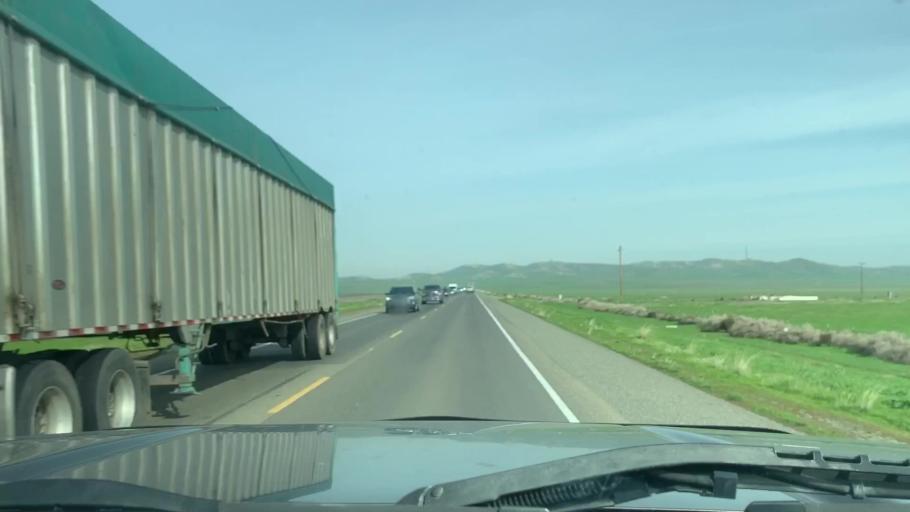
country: US
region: California
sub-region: Kings County
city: Avenal
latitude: 35.8308
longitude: -120.0910
